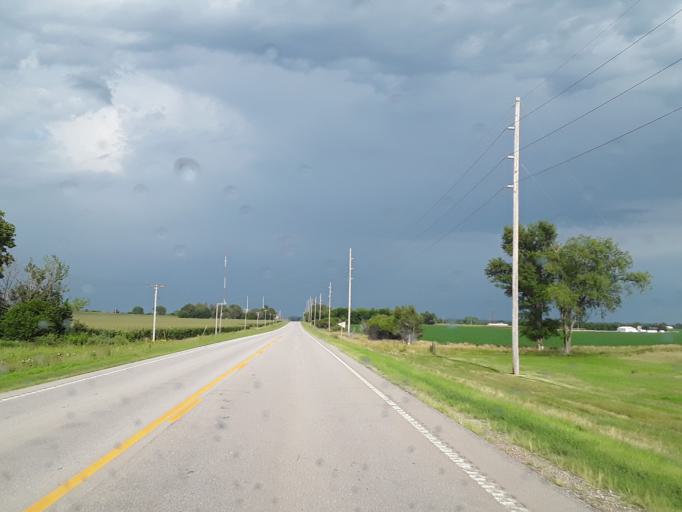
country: US
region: Nebraska
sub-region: Saunders County
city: Ashland
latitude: 41.0887
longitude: -96.3983
